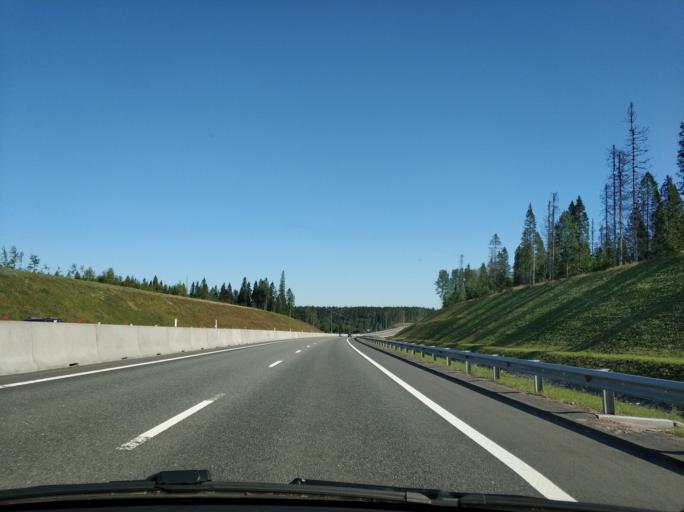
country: RU
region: Leningrad
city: Sosnovo
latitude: 60.4518
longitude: 30.1990
